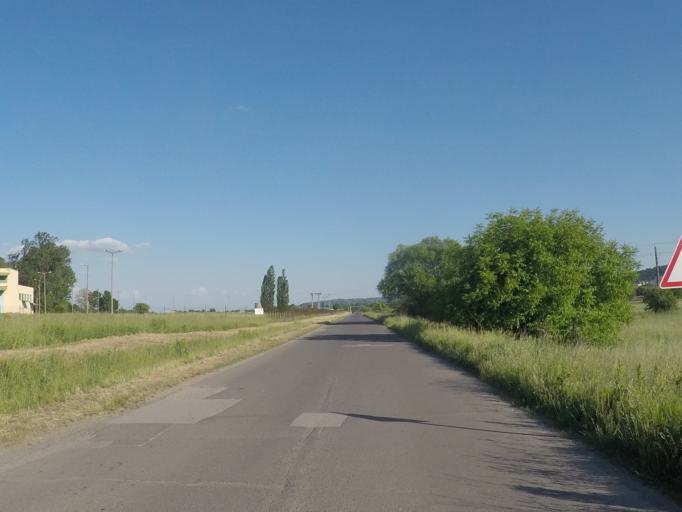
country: HU
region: Borsod-Abauj-Zemplen
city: Kazincbarcika
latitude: 48.2544
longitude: 20.6559
